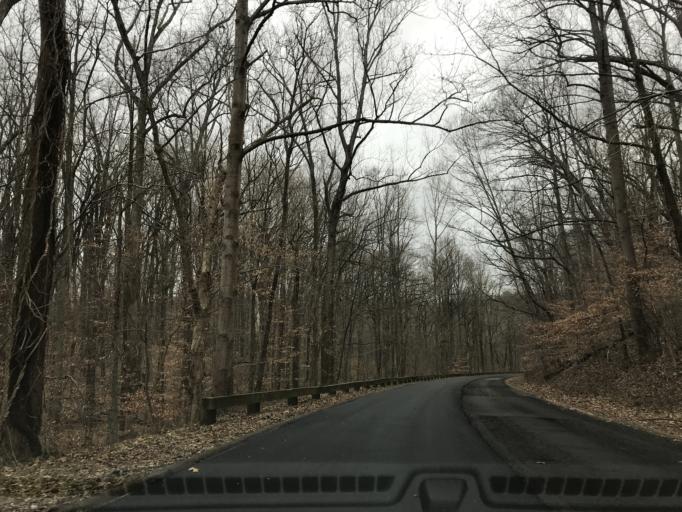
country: US
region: Maryland
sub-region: Montgomery County
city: Cabin John
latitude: 38.9607
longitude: -77.1540
